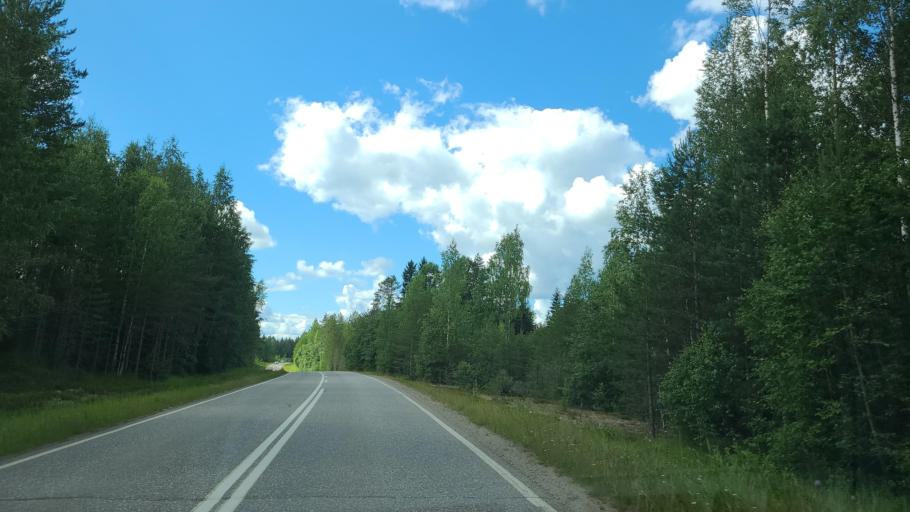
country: FI
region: Northern Savo
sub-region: Koillis-Savo
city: Kaavi
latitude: 62.9873
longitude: 28.8187
